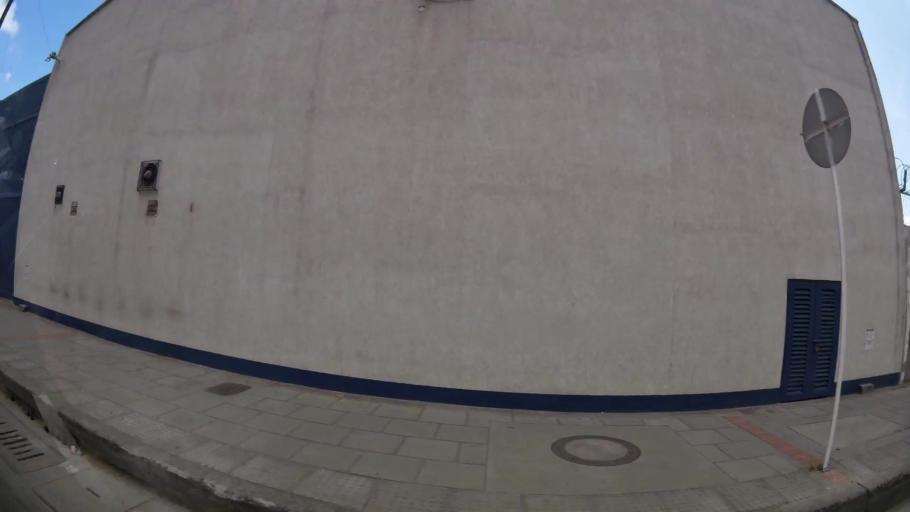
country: CO
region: Bogota D.C.
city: Bogota
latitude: 4.6309
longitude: -74.0991
